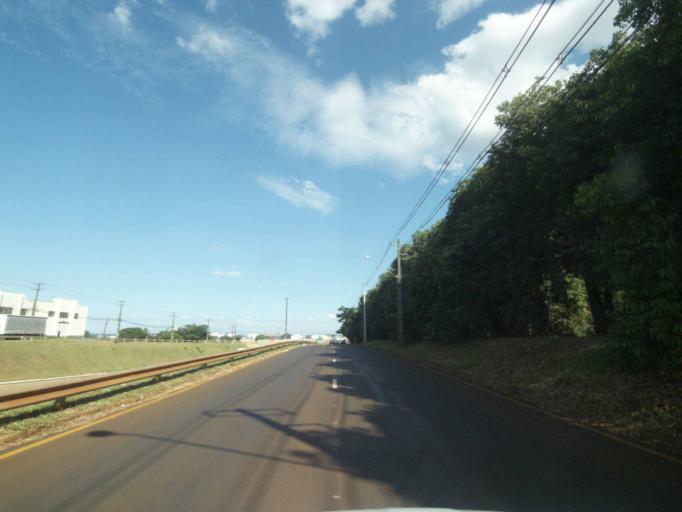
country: BR
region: Parana
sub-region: Londrina
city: Londrina
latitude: -23.3489
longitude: -51.1692
